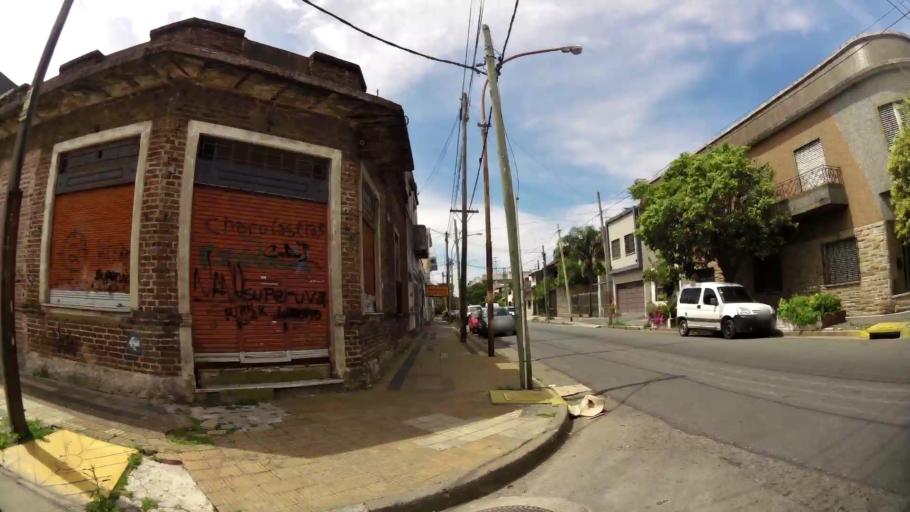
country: AR
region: Buenos Aires
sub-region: Partido de Lanus
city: Lanus
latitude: -34.6724
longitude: -58.4044
